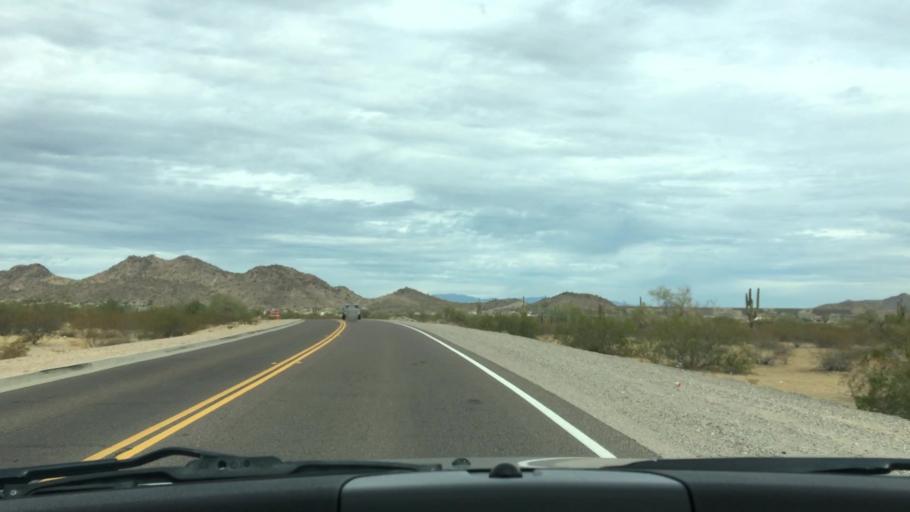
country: US
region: Arizona
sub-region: Maricopa County
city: Sun City West
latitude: 33.7176
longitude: -112.2328
